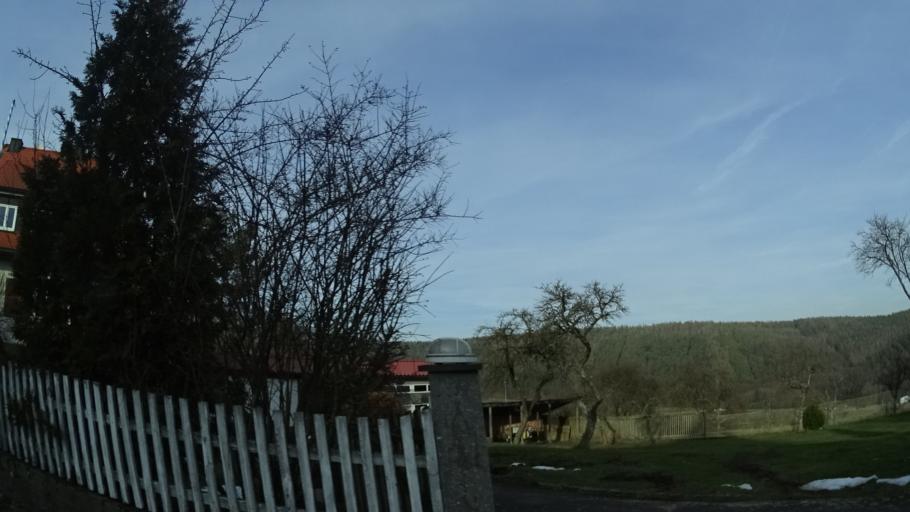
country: DE
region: Bavaria
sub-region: Regierungsbezirk Unterfranken
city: Sandberg
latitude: 50.3466
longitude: 10.0105
